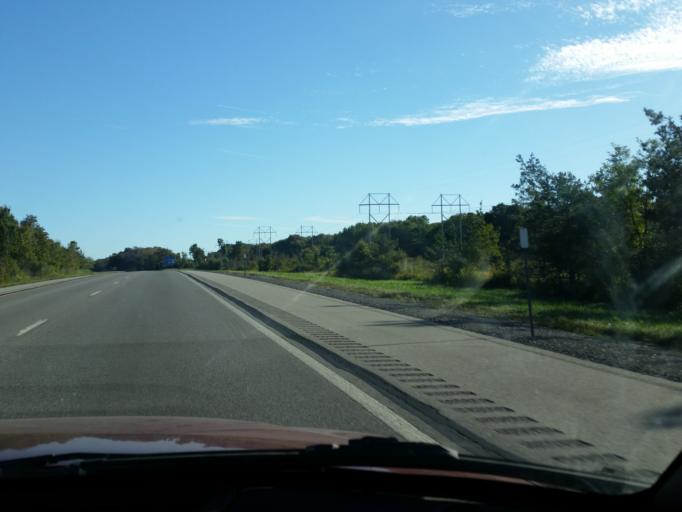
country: US
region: New York
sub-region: Erie County
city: Angola
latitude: 42.6149
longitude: -79.0141
